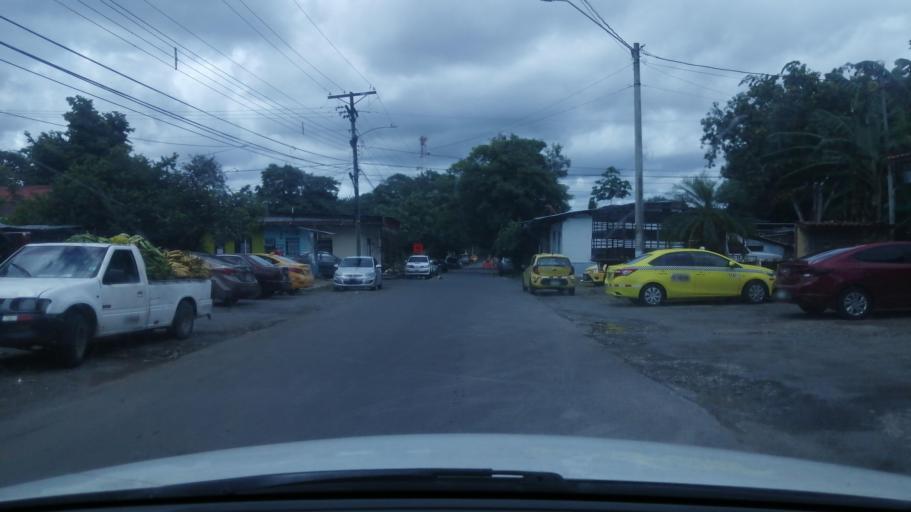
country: PA
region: Chiriqui
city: David
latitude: 8.4259
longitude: -82.4241
